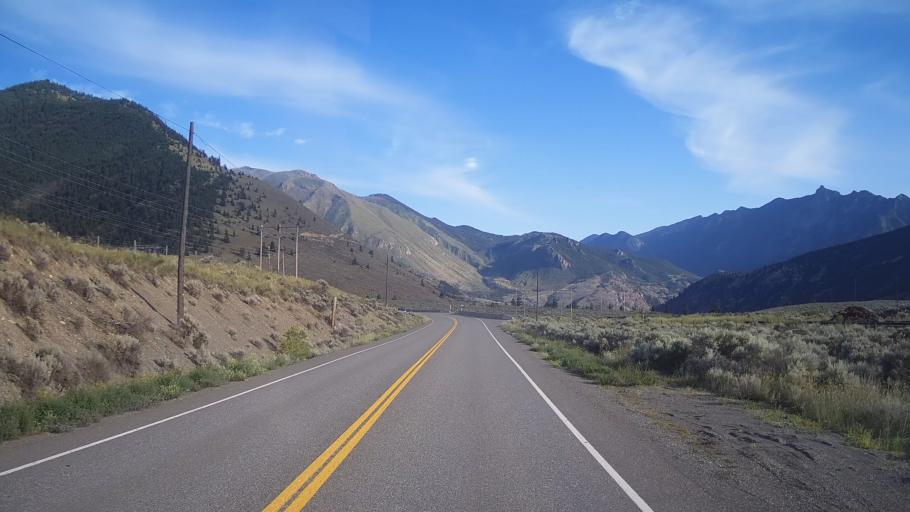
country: CA
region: British Columbia
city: Lillooet
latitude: 50.7998
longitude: -121.8446
